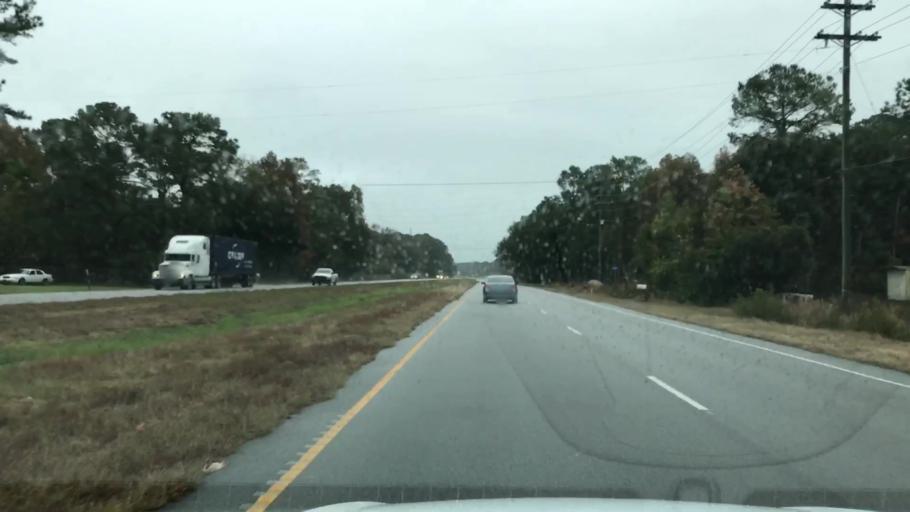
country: US
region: South Carolina
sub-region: Charleston County
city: Isle of Palms
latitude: 32.8931
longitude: -79.7378
